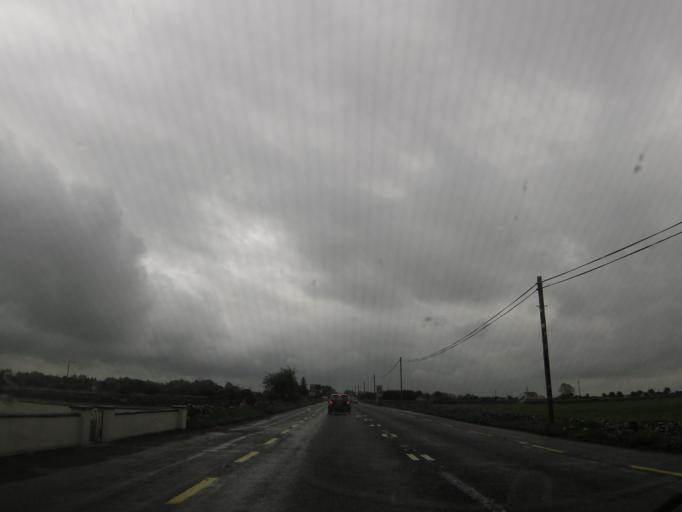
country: IE
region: Connaught
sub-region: County Galway
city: Claregalway
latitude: 53.3945
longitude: -8.9133
